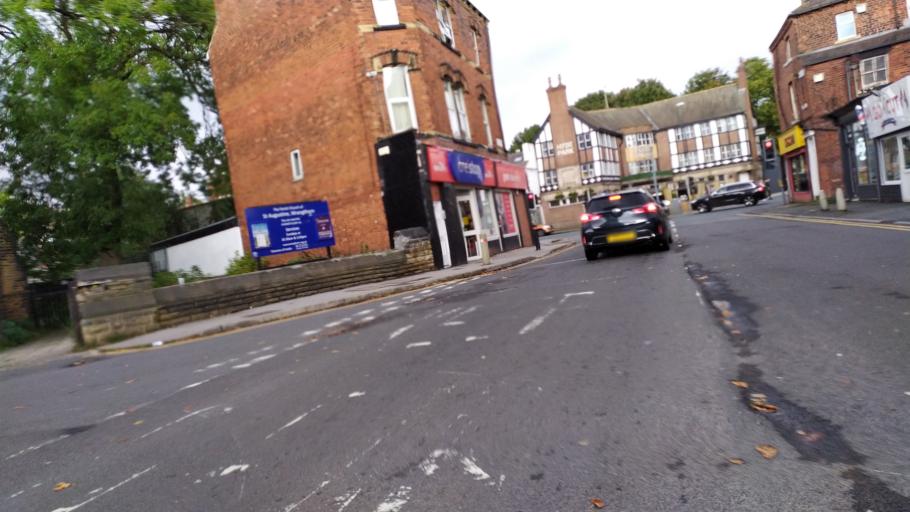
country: GB
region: England
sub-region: City and Borough of Leeds
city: Leeds
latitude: 53.8143
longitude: -1.5622
